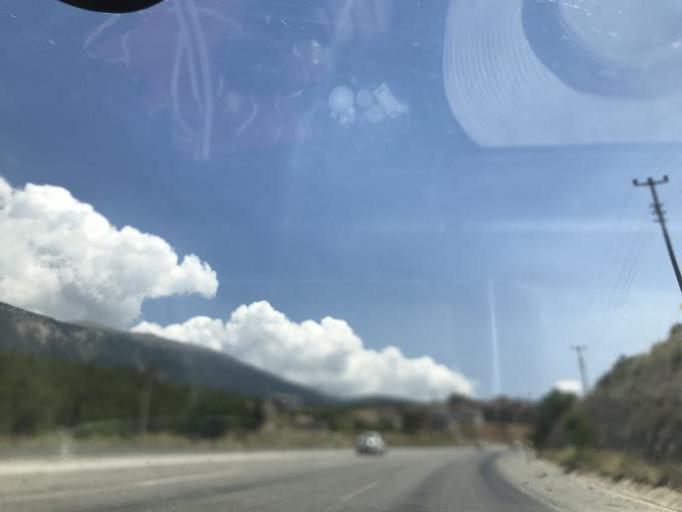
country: TR
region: Denizli
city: Honaz
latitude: 37.6922
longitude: 29.2144
